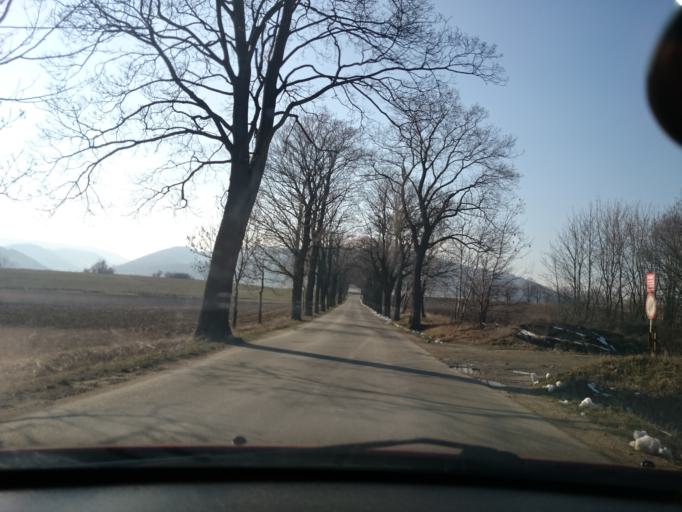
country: PL
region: Lower Silesian Voivodeship
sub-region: Powiat klodzki
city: Bystrzyca Klodzka
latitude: 50.3074
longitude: 16.6278
